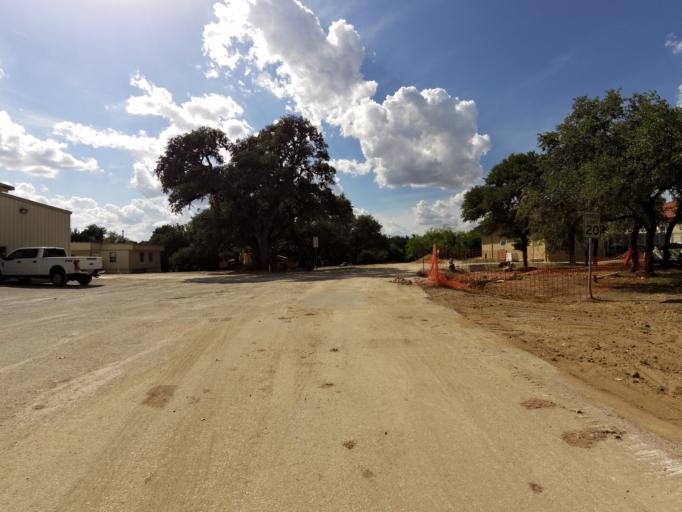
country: US
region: Texas
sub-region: Bexar County
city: Helotes
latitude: 29.5834
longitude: -98.6299
